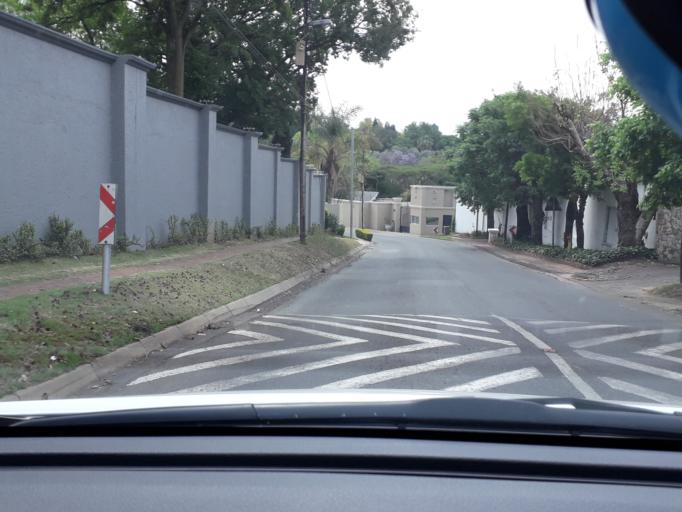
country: ZA
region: Gauteng
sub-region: City of Johannesburg Metropolitan Municipality
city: Johannesburg
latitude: -26.1198
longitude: 28.0641
